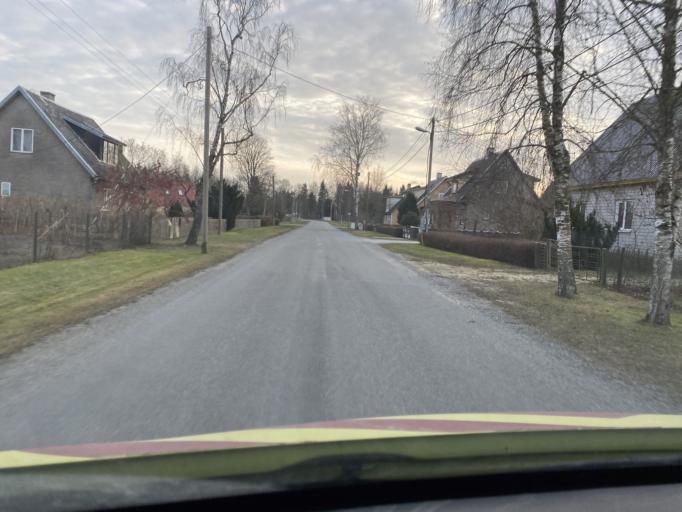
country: EE
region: Jogevamaa
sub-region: Poltsamaa linn
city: Poltsamaa
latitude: 58.6446
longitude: 25.9739
